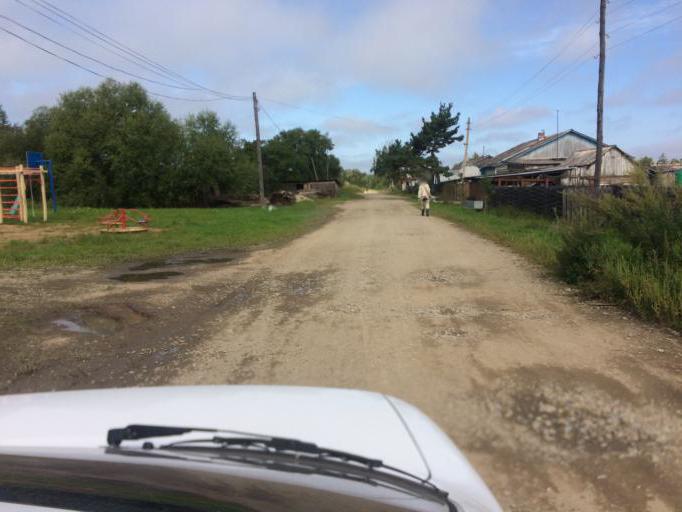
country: RU
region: Primorskiy
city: Dal'nerechensk
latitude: 45.9182
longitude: 133.7241
